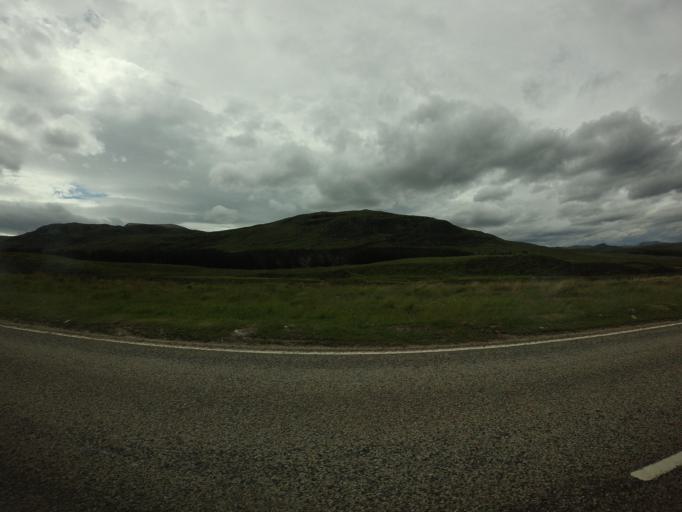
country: GB
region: Scotland
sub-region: Highland
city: Ullapool
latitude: 57.7487
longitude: -4.9874
